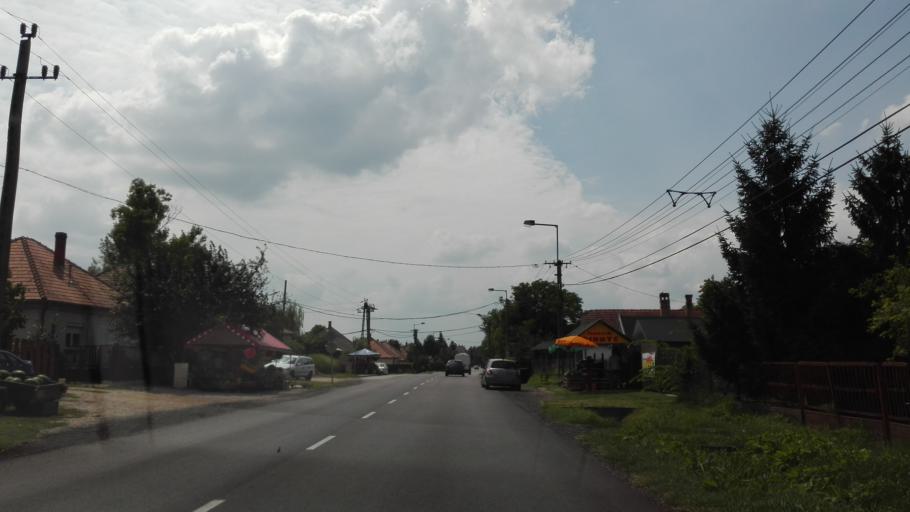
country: HU
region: Fejer
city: Cece
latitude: 46.7734
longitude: 18.6397
